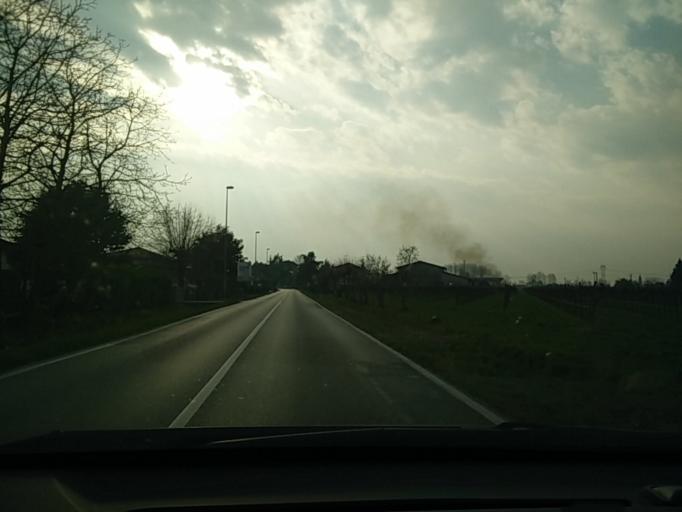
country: IT
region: Veneto
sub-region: Provincia di Treviso
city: Vazzola
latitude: 45.8412
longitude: 12.3796
